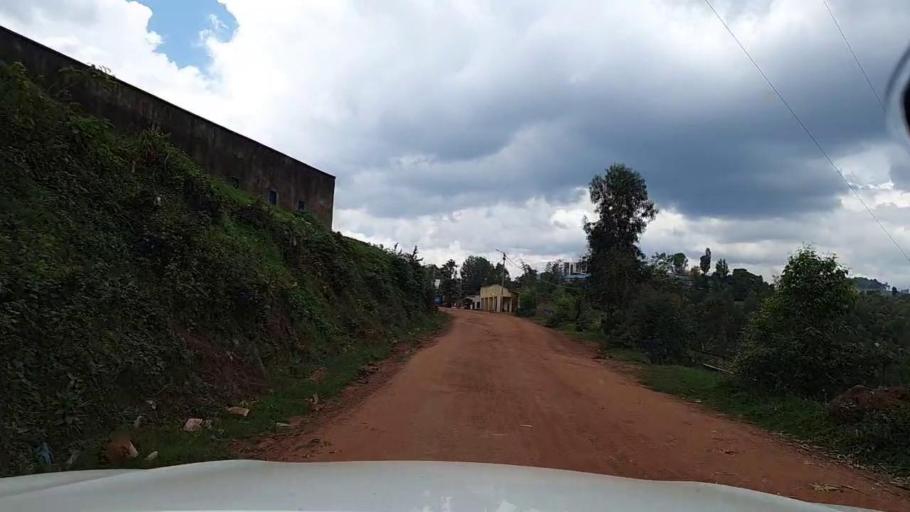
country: BI
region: Kayanza
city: Kayanza
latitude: -2.7130
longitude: 29.5383
